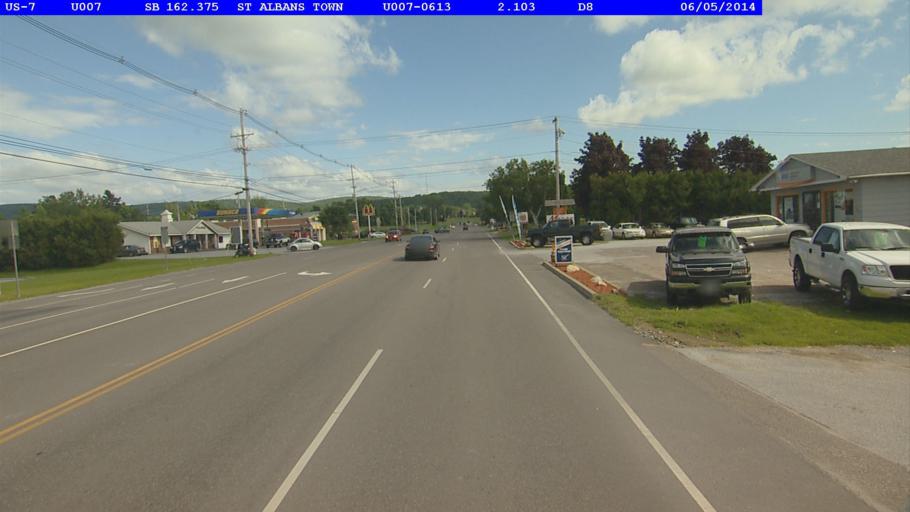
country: US
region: Vermont
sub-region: Franklin County
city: Saint Albans
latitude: 44.8386
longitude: -73.0821
